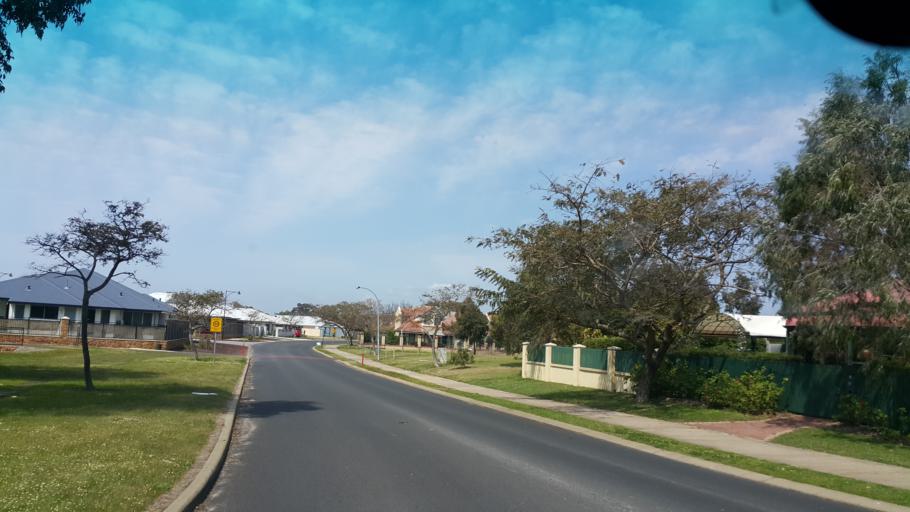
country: AU
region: Western Australia
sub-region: Busselton
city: Quindalup
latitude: -33.6227
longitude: 115.1074
